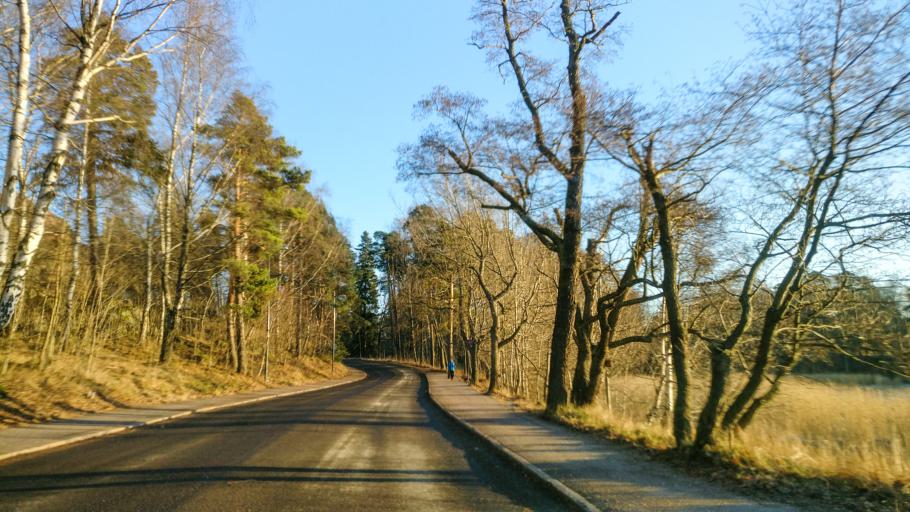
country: FI
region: Uusimaa
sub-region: Helsinki
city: Helsinki
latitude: 60.1877
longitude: 24.8923
